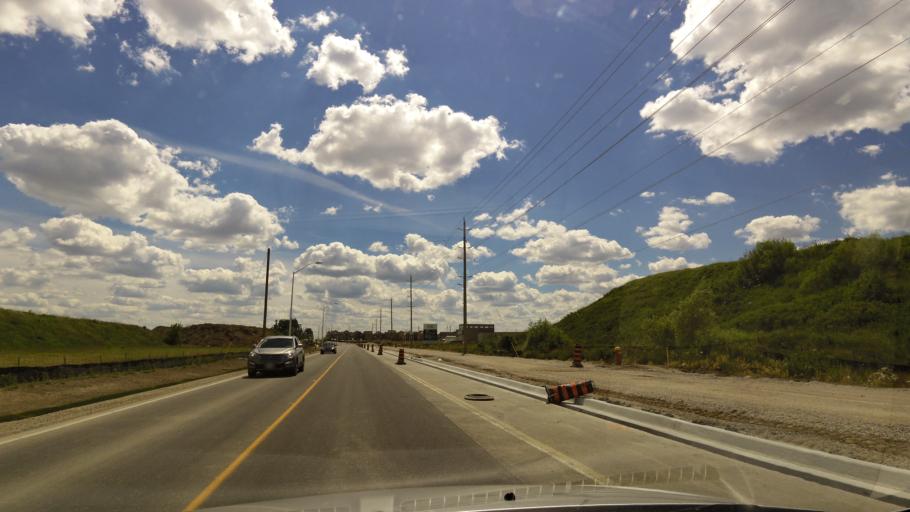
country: CA
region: Ontario
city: Brampton
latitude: 43.6354
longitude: -79.8655
